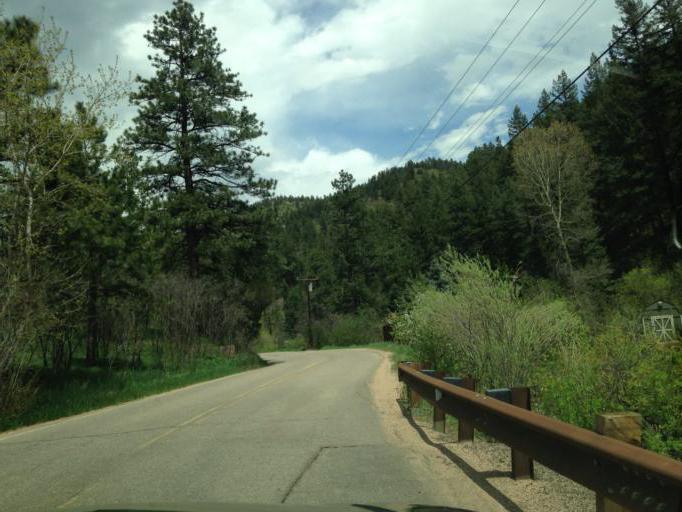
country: US
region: Colorado
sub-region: Jefferson County
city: Ken Caryl
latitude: 39.5191
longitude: -105.1861
